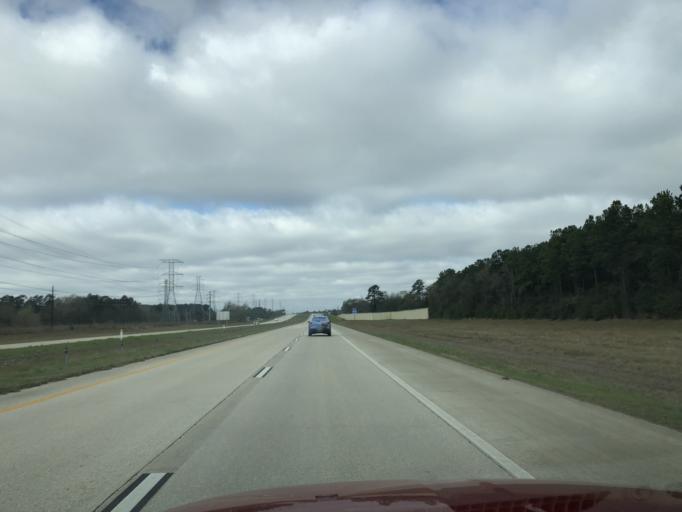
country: US
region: Texas
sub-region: Harris County
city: Spring
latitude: 30.0917
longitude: -95.4713
